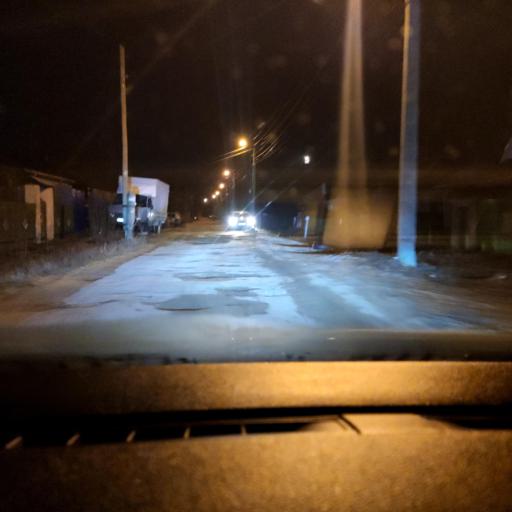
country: RU
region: Voronezj
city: Pridonskoy
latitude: 51.6887
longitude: 39.0578
